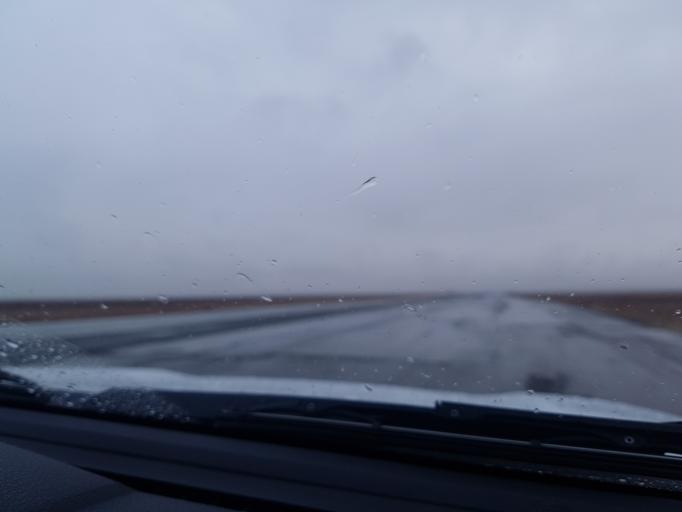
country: TM
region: Balkan
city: Turkmenbasy
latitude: 40.0236
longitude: 53.6774
